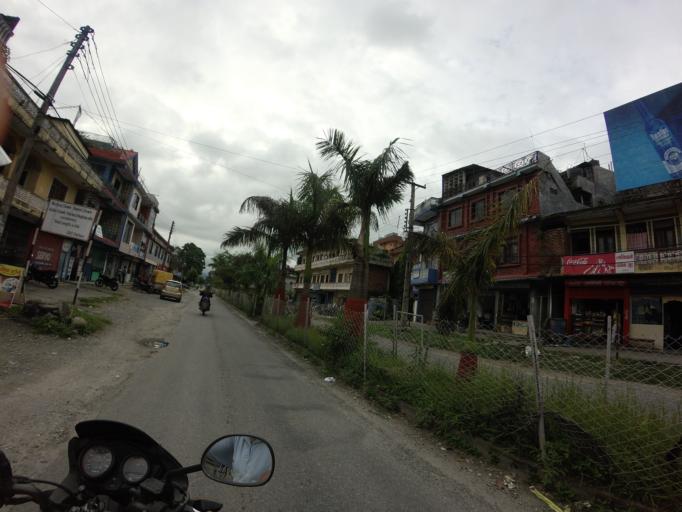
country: NP
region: Western Region
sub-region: Gandaki Zone
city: Pokhara
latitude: 28.1985
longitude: 83.9755
